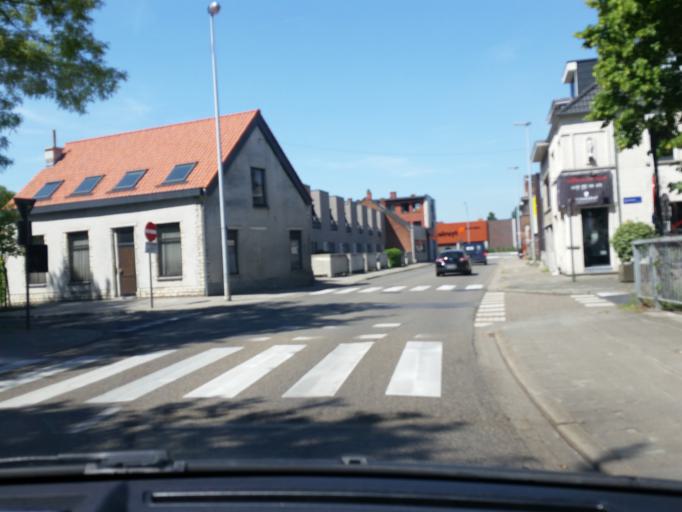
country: BE
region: Flanders
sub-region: Provincie Antwerpen
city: Bonheiden
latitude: 51.0336
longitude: 4.5139
